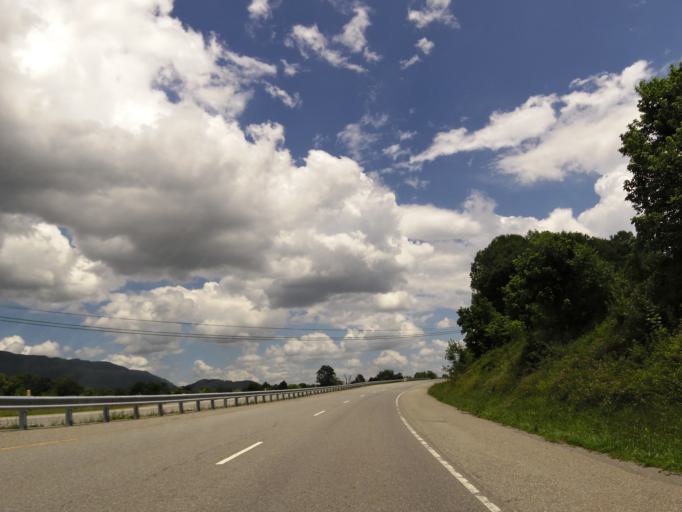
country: US
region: Tennessee
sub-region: Claiborne County
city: Harrogate
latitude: 36.6298
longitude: -83.5220
